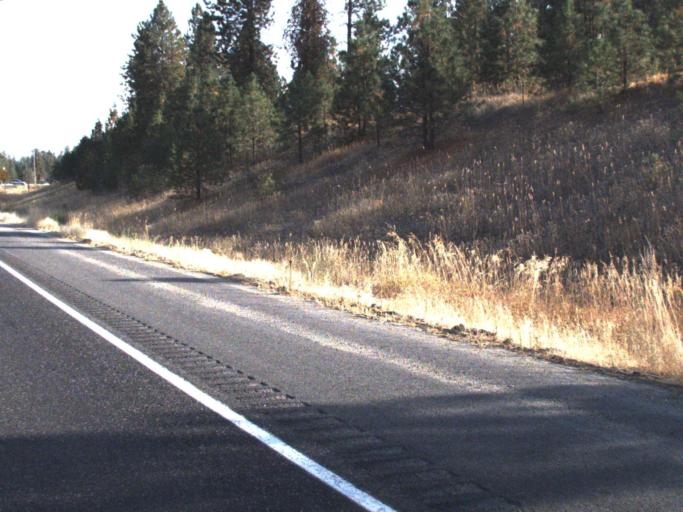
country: US
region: Washington
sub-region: Spokane County
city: Mead
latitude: 47.8273
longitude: -117.3492
